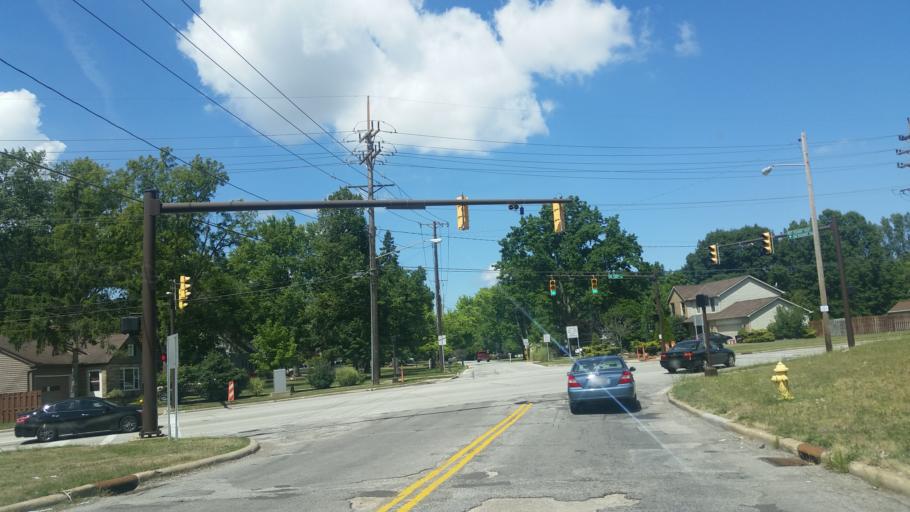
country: US
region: Ohio
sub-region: Cuyahoga County
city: Middleburg Heights
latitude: 41.3661
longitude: -81.7844
